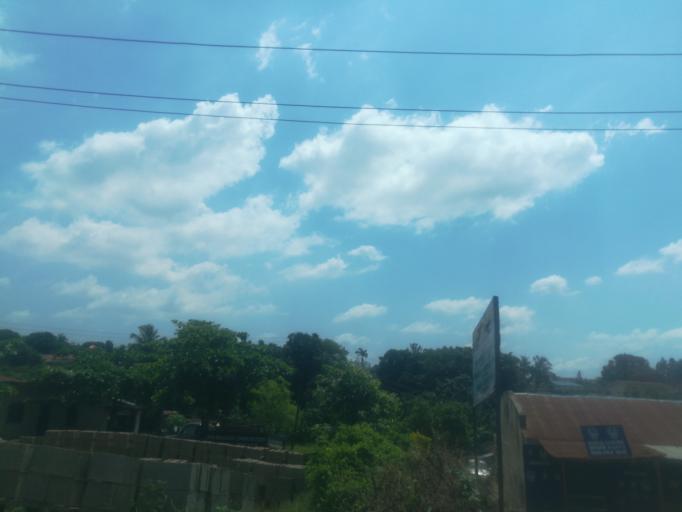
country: NG
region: Oyo
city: Ibadan
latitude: 7.3823
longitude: 3.8699
